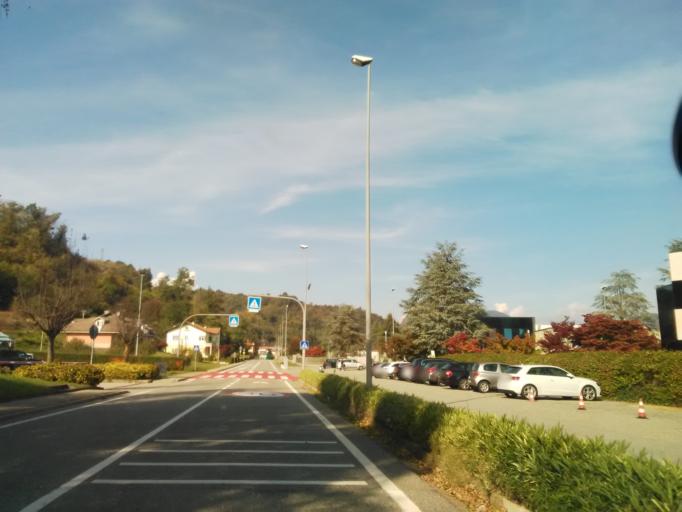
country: IT
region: Piedmont
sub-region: Provincia di Novara
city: Grignasco
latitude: 45.6589
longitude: 8.3354
